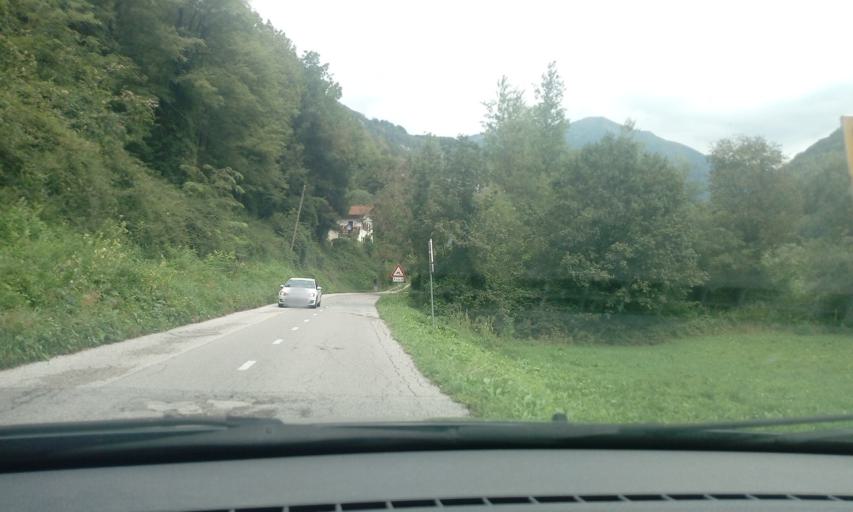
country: SI
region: Tolmin
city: Tolmin
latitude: 46.1469
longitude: 13.7684
